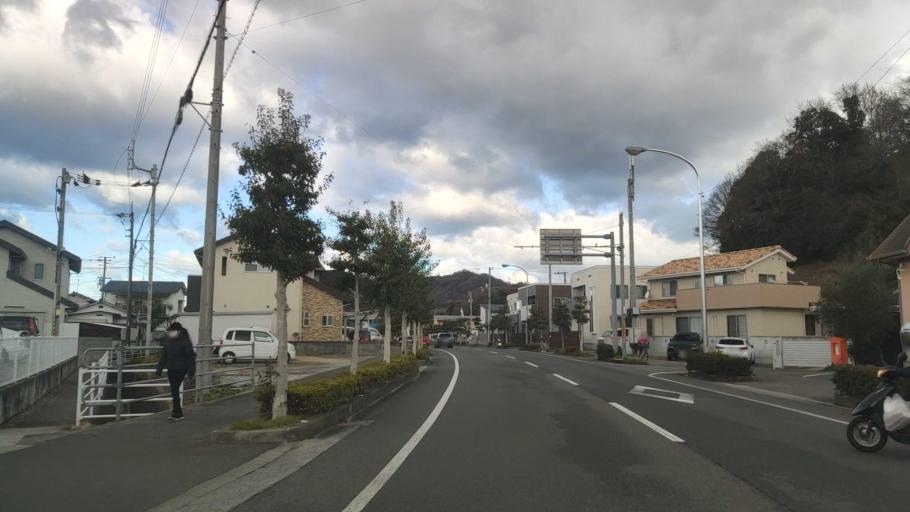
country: JP
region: Ehime
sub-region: Shikoku-chuo Shi
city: Matsuyama
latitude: 33.8684
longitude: 132.7241
